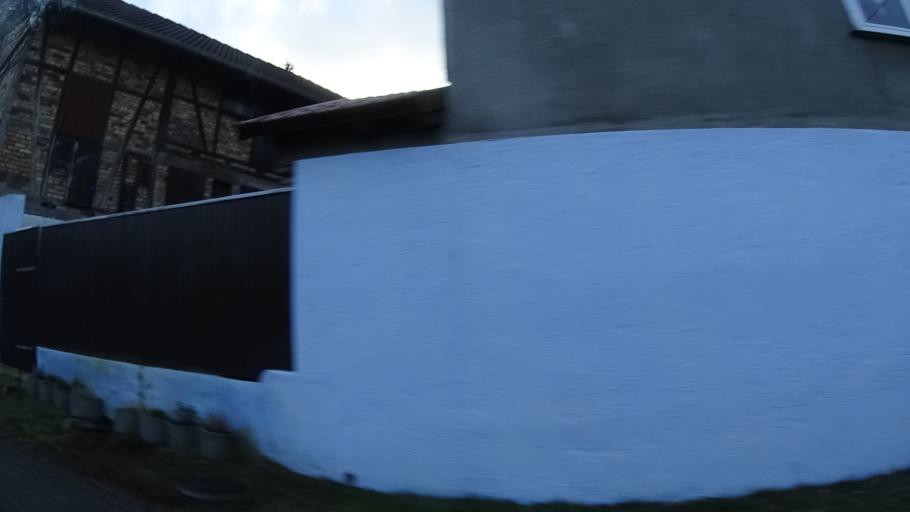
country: DE
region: Thuringia
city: Behringen
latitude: 50.7337
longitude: 11.0360
